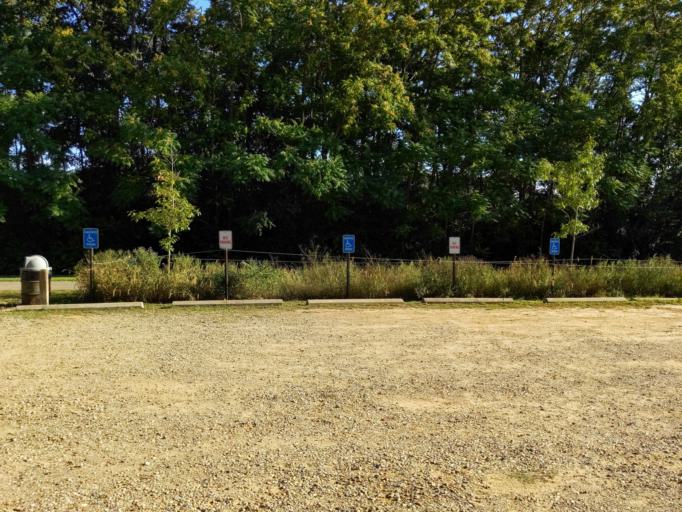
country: US
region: Michigan
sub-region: Jackson County
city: Spring Arbor
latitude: 42.1869
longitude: -84.5583
